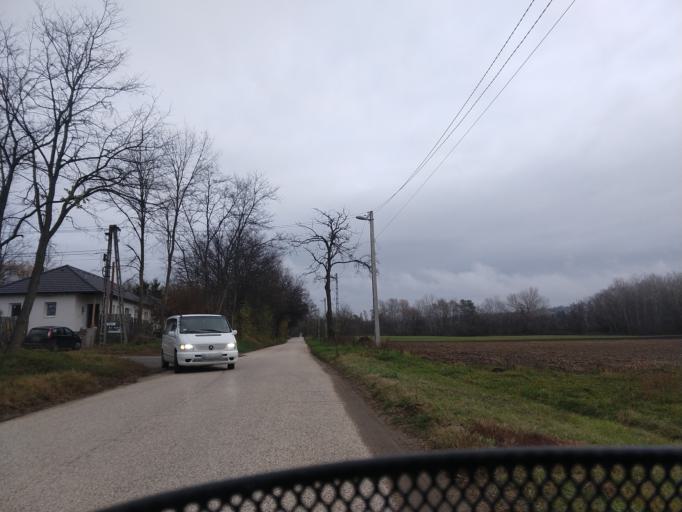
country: HU
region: Pest
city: Erdokertes
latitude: 47.6656
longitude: 19.2904
